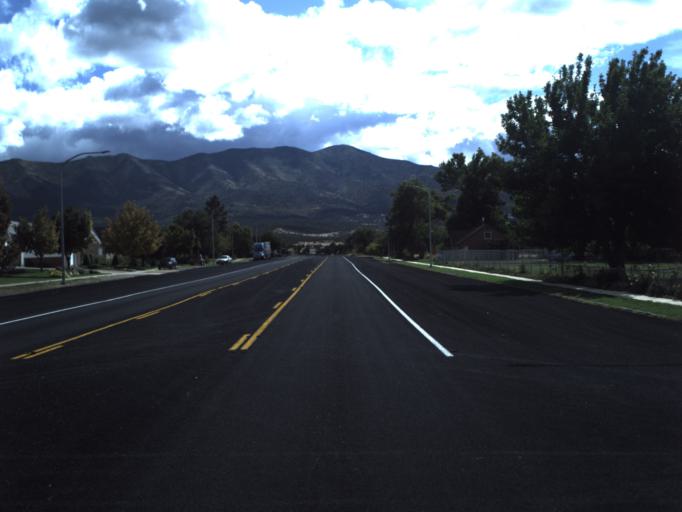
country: US
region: Utah
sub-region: Millard County
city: Fillmore
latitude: 38.7969
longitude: -112.4377
